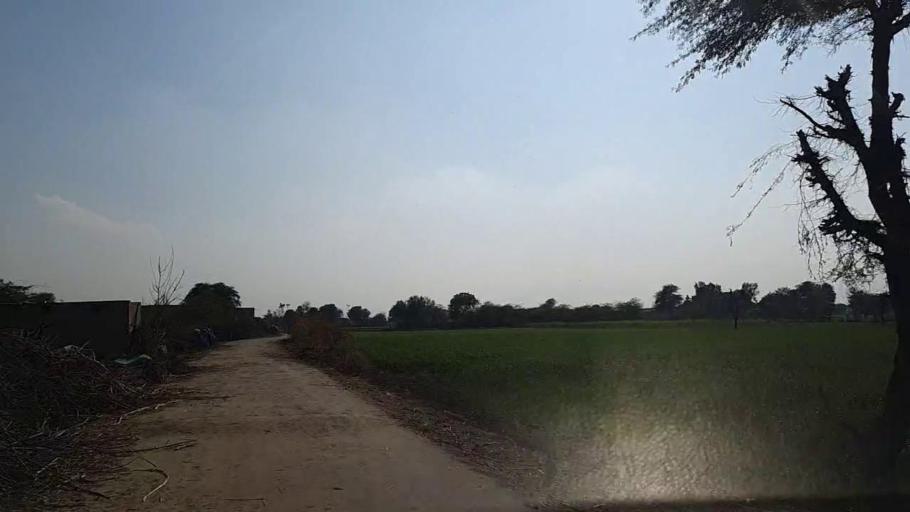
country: PK
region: Sindh
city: Jam Sahib
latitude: 26.2779
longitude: 68.6111
